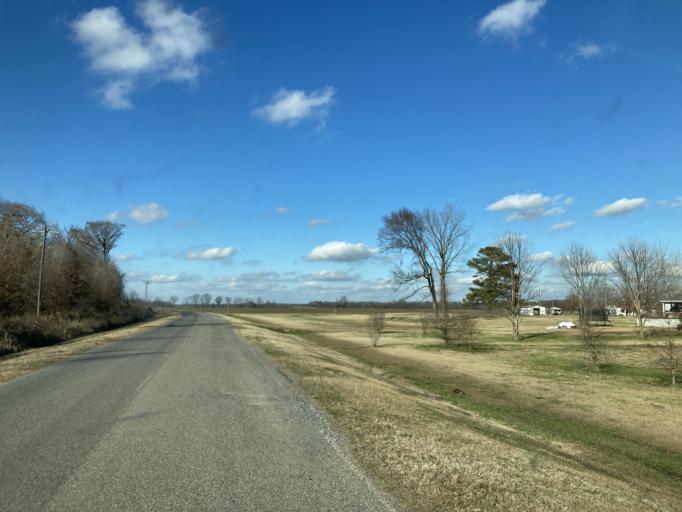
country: US
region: Mississippi
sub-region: Yazoo County
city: Yazoo City
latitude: 32.9335
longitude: -90.4731
